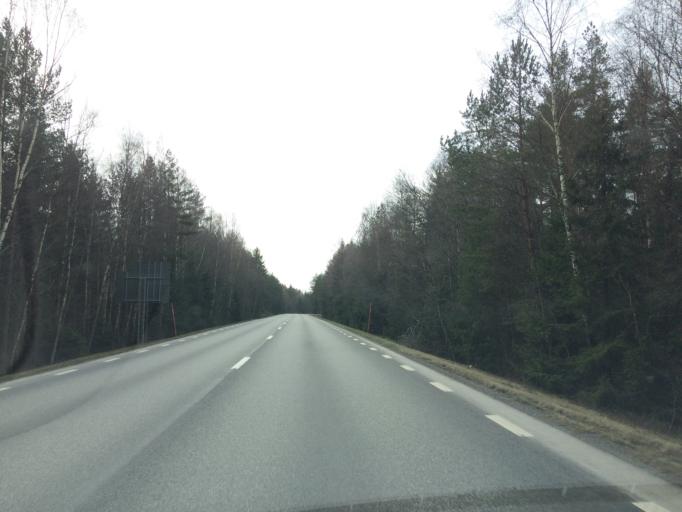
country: SE
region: Skane
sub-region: Osby Kommun
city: Lonsboda
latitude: 56.3874
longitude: 14.2761
